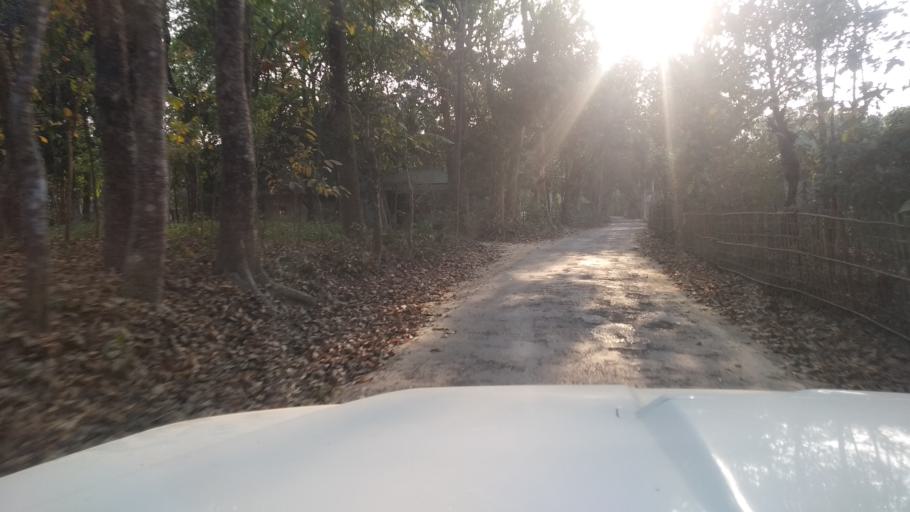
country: IN
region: Tripura
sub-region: West Tripura
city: Sonamura
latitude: 23.3259
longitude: 91.2991
